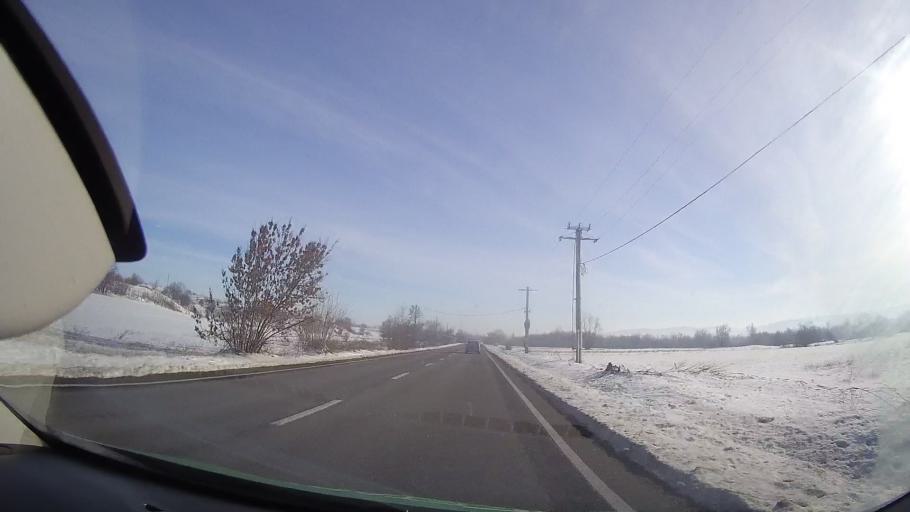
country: RO
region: Neamt
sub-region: Comuna Ghindaoani
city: Ghindaoani
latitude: 47.0775
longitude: 26.3508
